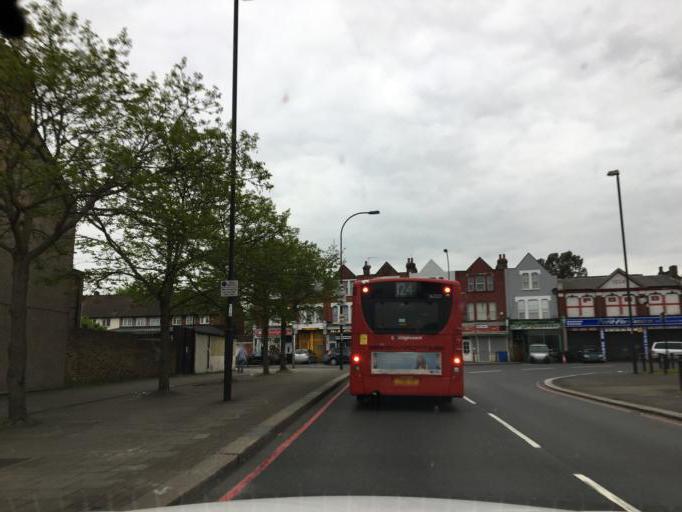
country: GB
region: England
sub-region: Greater London
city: Catford
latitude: 51.4443
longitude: -0.0178
